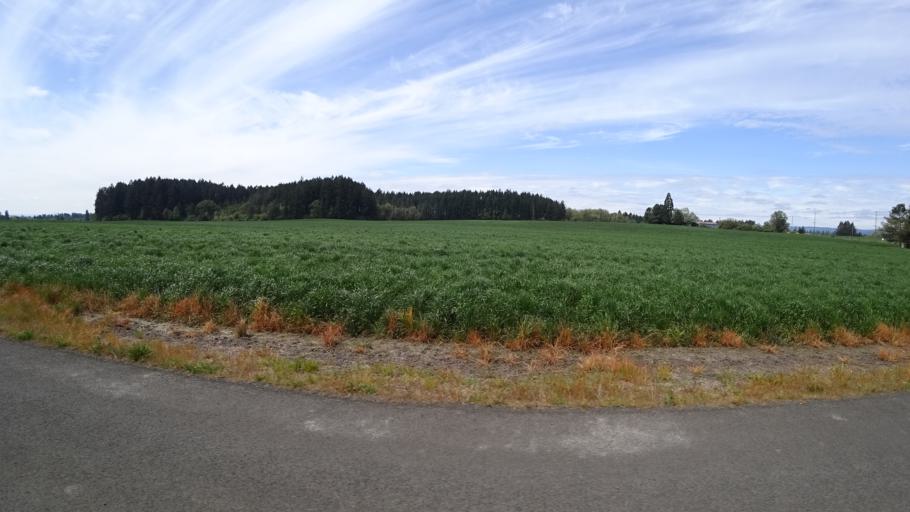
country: US
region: Oregon
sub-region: Washington County
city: North Plains
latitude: 45.5779
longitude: -122.9378
